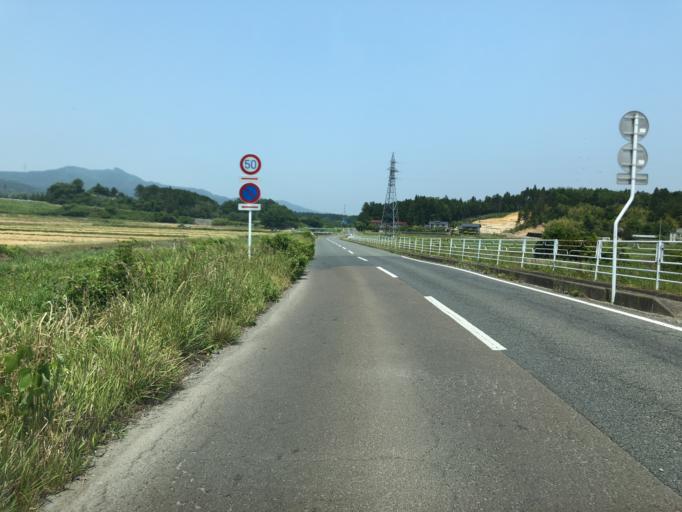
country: JP
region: Miyagi
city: Marumori
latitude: 37.8322
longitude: 140.8958
